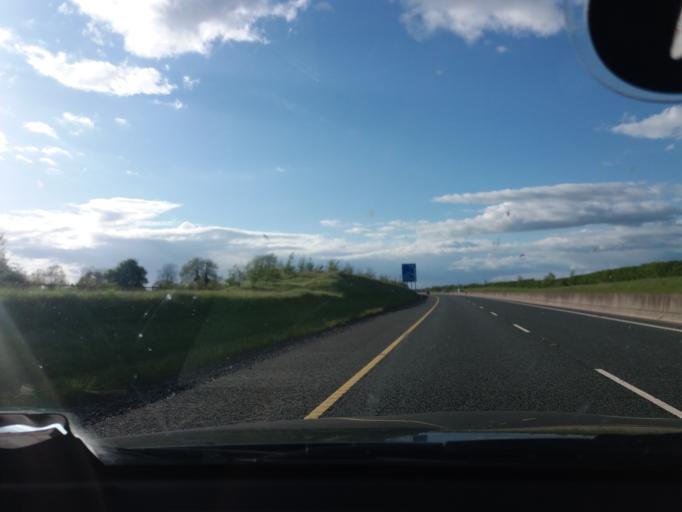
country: IE
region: Leinster
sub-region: Kildare
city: Castledermot
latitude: 52.8766
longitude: -6.8427
